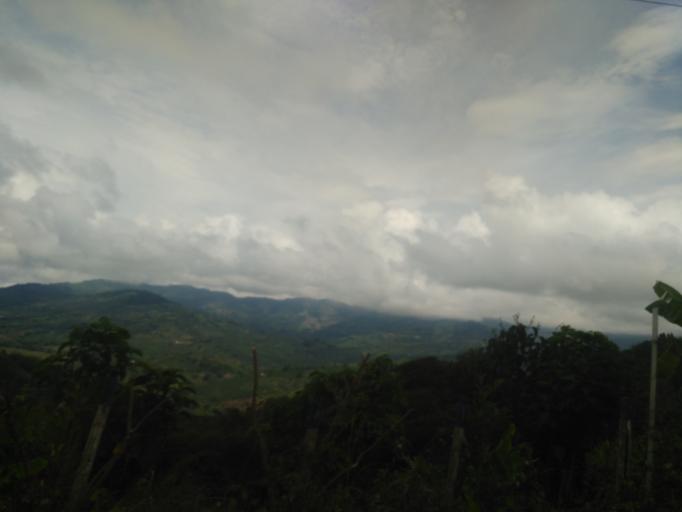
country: CO
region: Valle del Cauca
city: Sevilla
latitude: 4.2953
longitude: -75.9003
